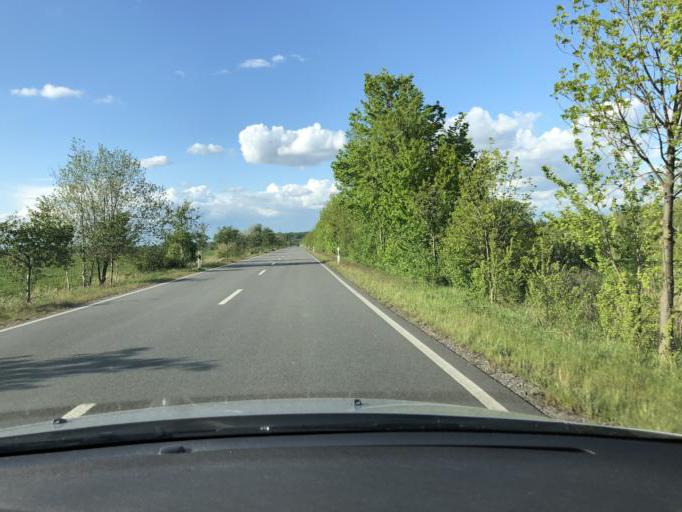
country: DE
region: Saxony
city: Neukieritzsch
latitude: 51.1682
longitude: 12.4179
